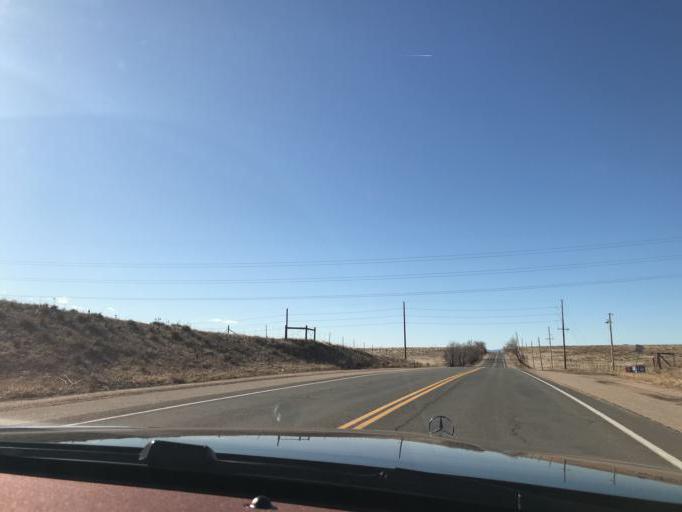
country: US
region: Colorado
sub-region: Boulder County
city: Superior
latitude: 39.8915
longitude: -105.1656
